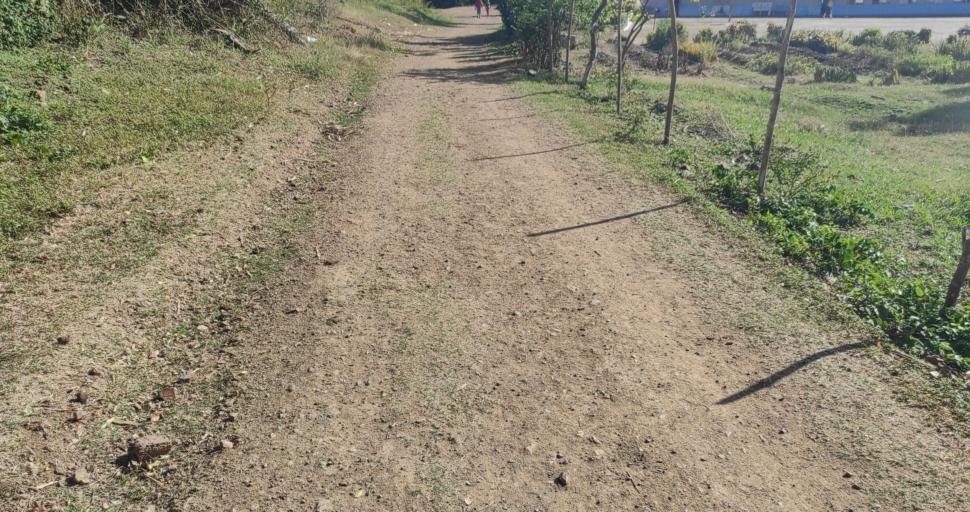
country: CU
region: Santiago de Cuba
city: Segundo Frente
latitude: 20.4380
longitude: -75.5041
